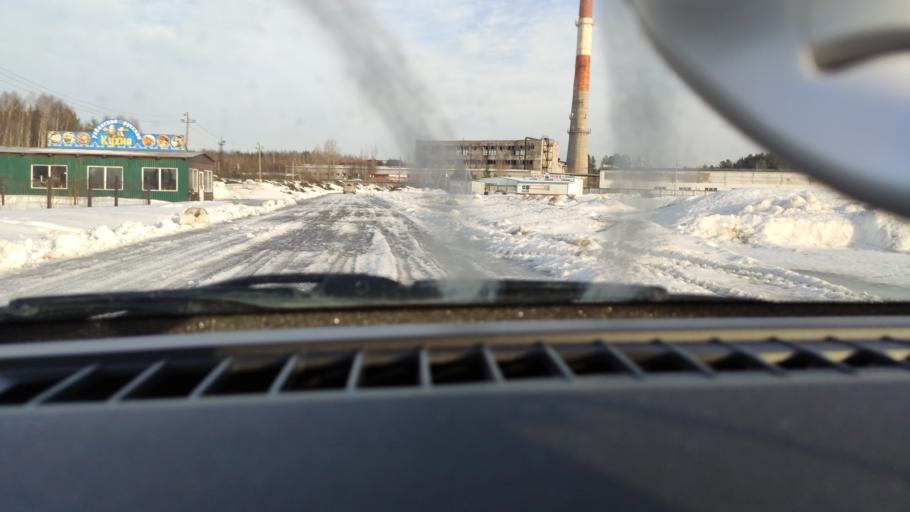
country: RU
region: Perm
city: Perm
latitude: 58.0374
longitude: 56.2031
